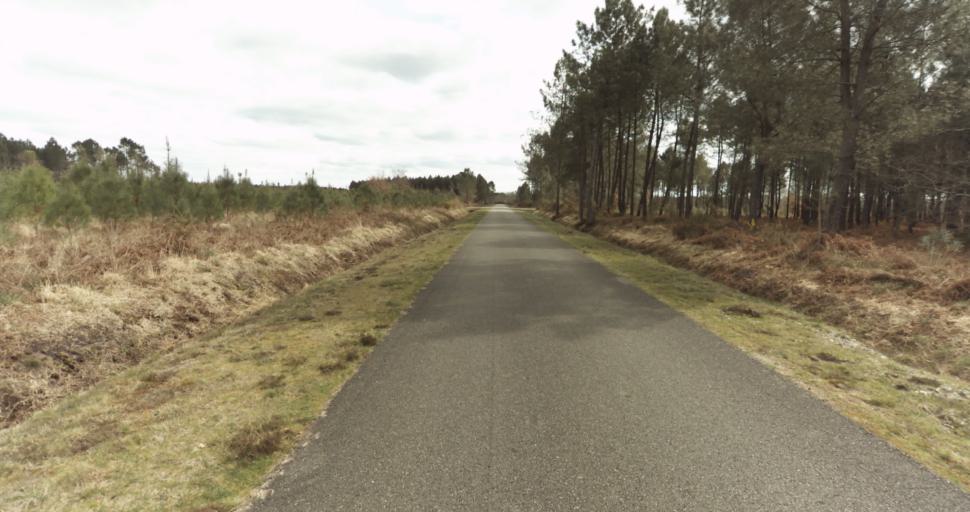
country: FR
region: Aquitaine
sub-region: Departement des Landes
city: Roquefort
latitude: 44.1053
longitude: -0.4403
